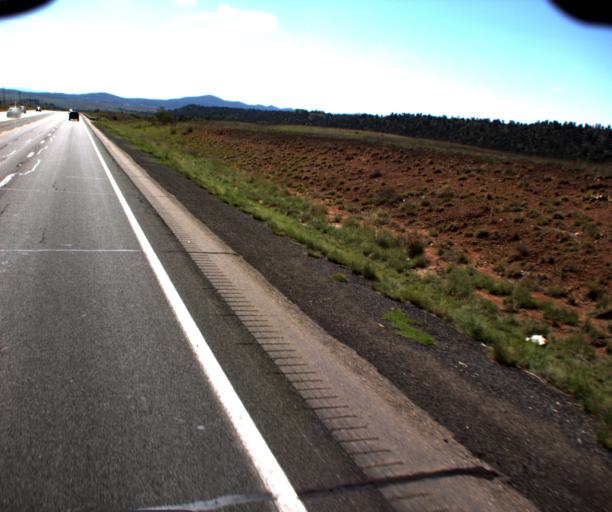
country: US
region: Arizona
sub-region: Yavapai County
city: Prescott Valley
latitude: 34.5776
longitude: -112.2924
